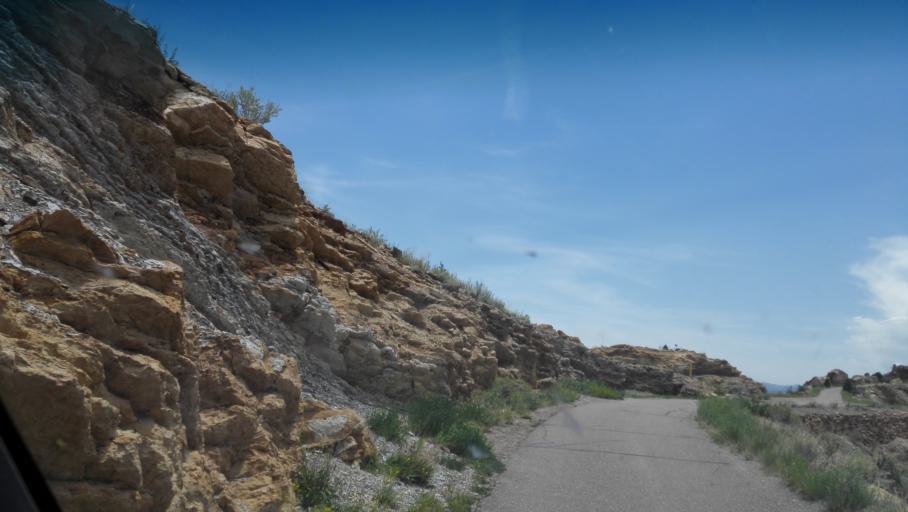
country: US
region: Colorado
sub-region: Fremont County
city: Canon City
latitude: 38.4626
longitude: -105.2520
